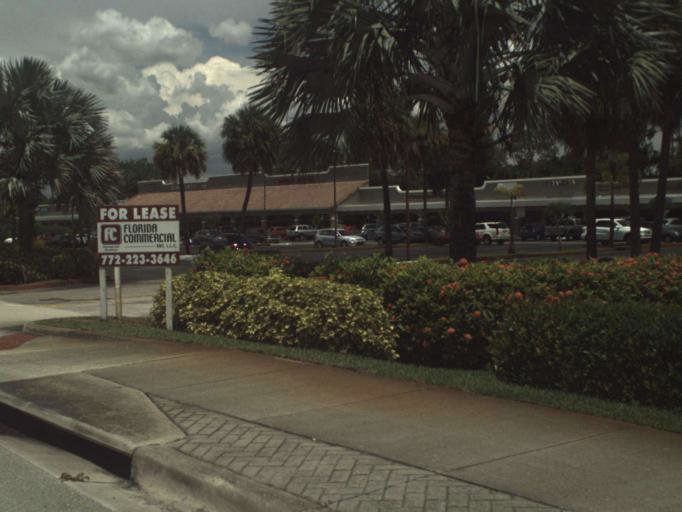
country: US
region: Florida
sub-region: Martin County
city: Sewall's Point
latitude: 27.1962
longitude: -80.2179
